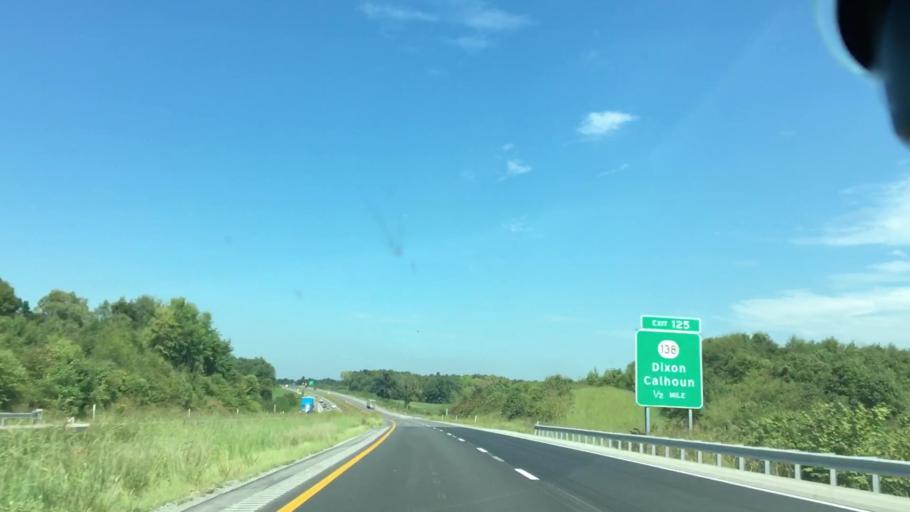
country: US
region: Kentucky
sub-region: Webster County
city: Sebree
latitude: 37.4751
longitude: -87.4767
